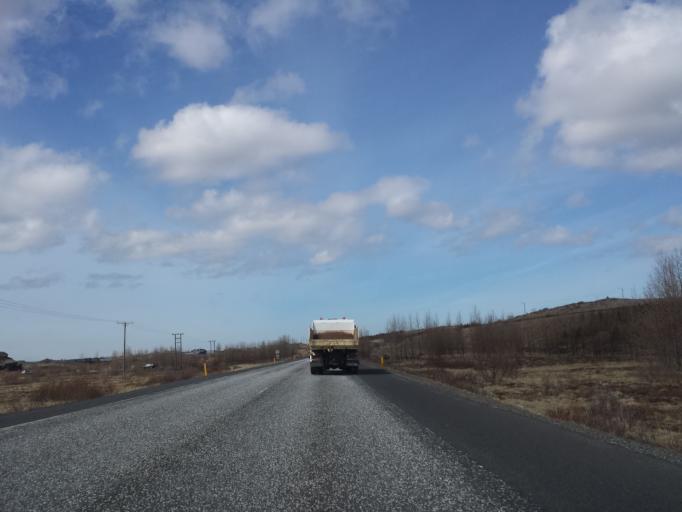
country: IS
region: Capital Region
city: Mosfellsbaer
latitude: 64.0951
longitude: -21.7361
